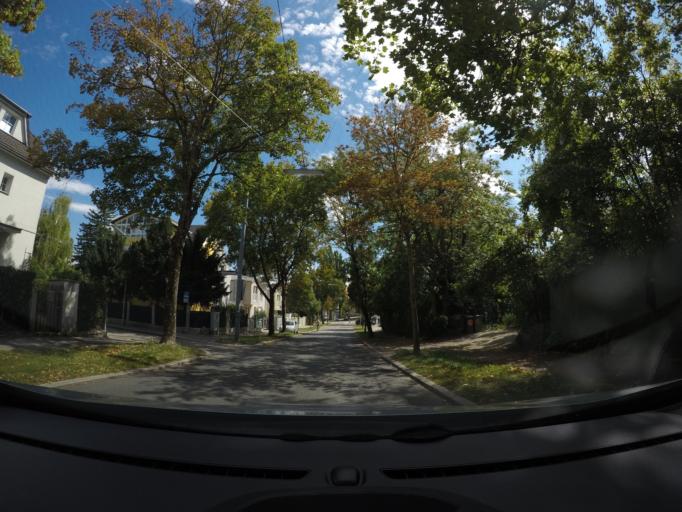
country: AT
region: Lower Austria
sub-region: Politischer Bezirk Modling
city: Perchtoldsdorf
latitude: 48.1820
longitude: 16.2646
